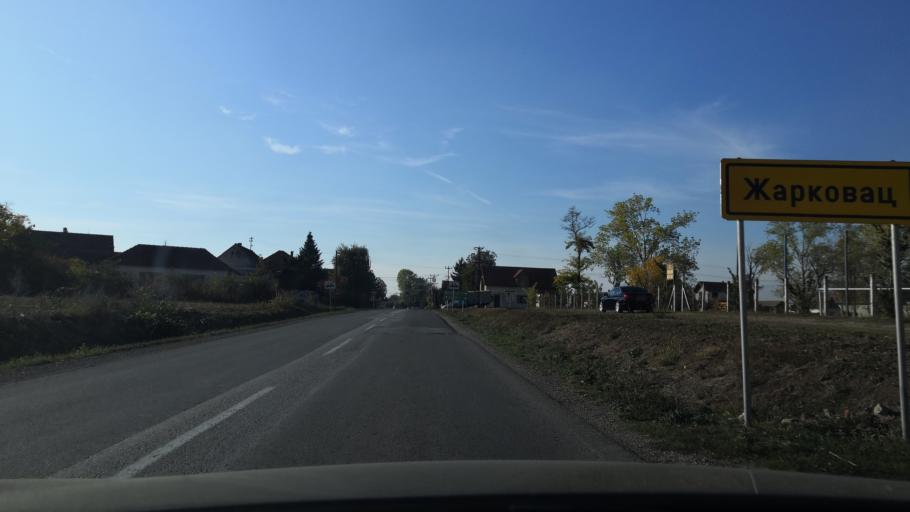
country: RS
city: Putinci
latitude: 45.0004
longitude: 19.9404
